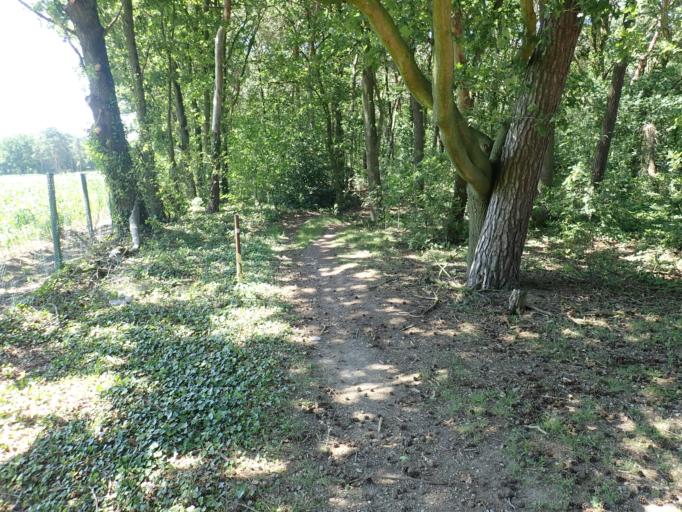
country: BE
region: Flanders
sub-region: Provincie Antwerpen
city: Beerse
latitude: 51.2940
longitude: 4.8223
